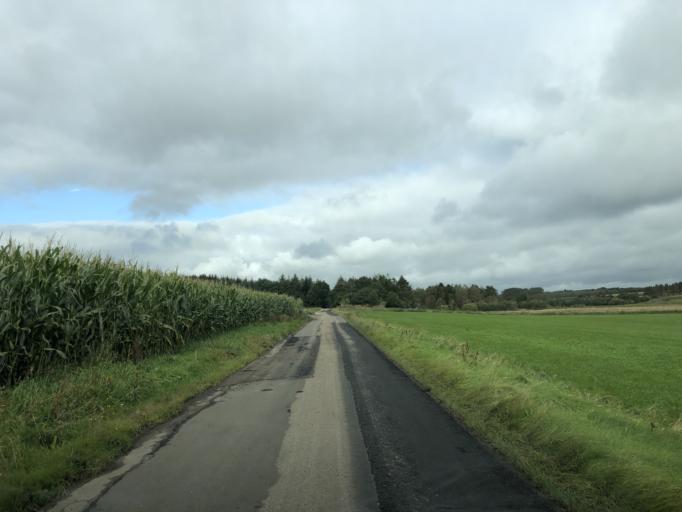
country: DK
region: Central Jutland
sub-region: Holstebro Kommune
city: Ulfborg
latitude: 56.3008
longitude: 8.4401
